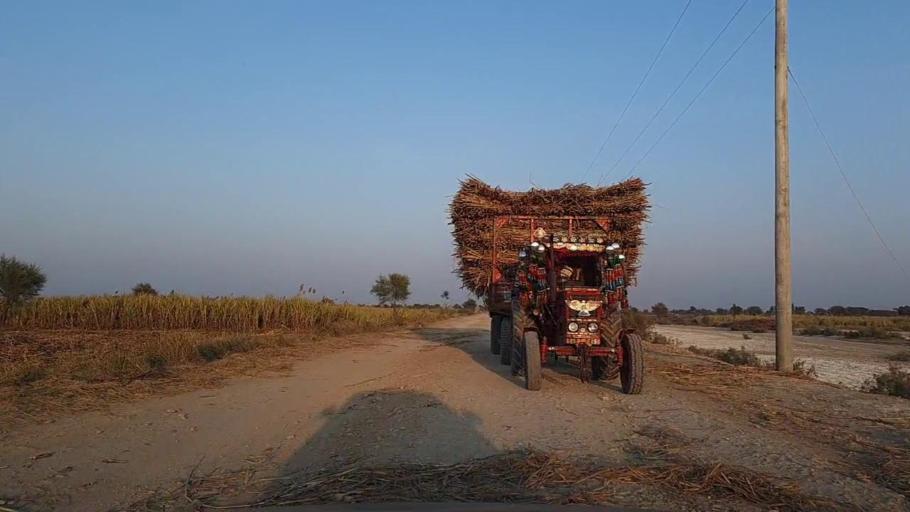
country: PK
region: Sindh
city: Tando Mittha Khan
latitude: 25.9654
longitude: 69.0709
